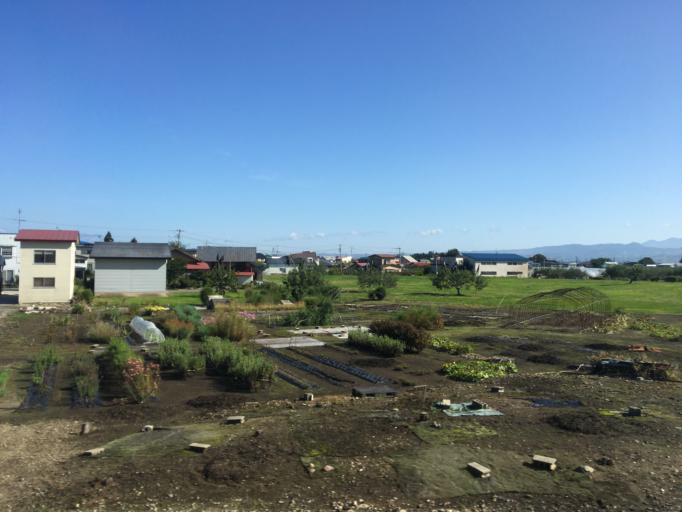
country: JP
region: Aomori
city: Hirosaki
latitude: 40.5766
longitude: 140.4993
